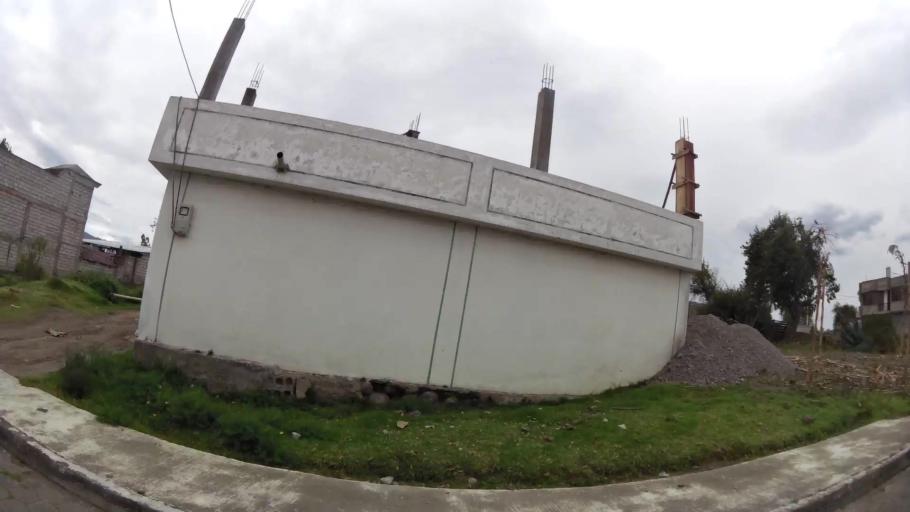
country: EC
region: Cotopaxi
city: Latacunga
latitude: -0.9578
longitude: -78.6068
